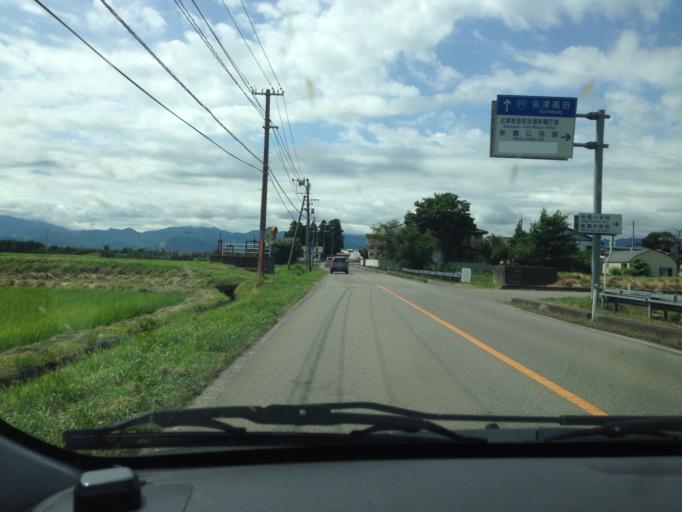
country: JP
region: Fukushima
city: Kitakata
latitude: 37.5111
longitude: 139.8344
